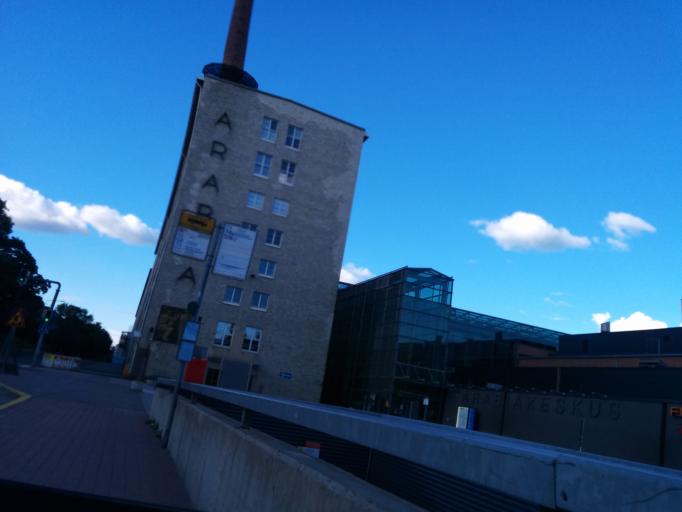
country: FI
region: Uusimaa
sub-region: Helsinki
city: Helsinki
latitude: 60.2081
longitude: 24.9750
